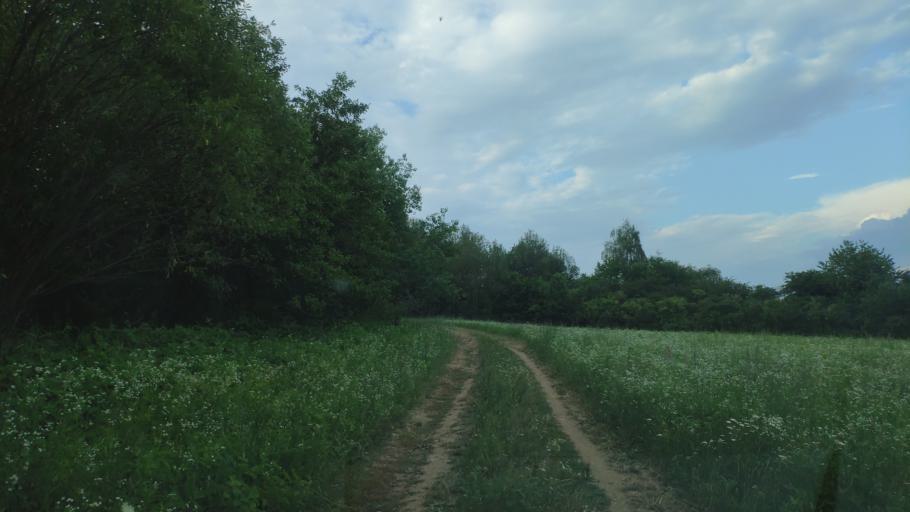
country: SK
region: Kosicky
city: Moldava nad Bodvou
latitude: 48.7067
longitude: 20.9896
